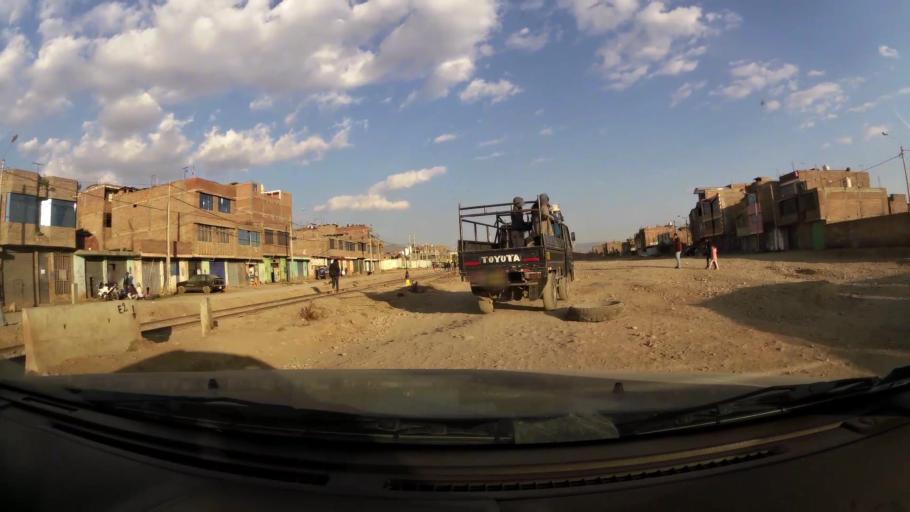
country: PE
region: Junin
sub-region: Provincia de Huancayo
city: Pilcomay
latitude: -12.0342
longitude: -75.2290
